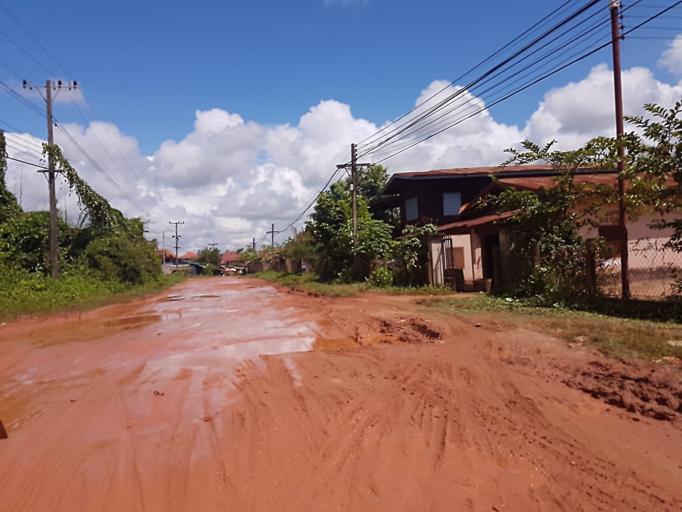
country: TH
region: Nong Khai
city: Nong Khai
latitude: 17.9526
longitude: 102.7030
